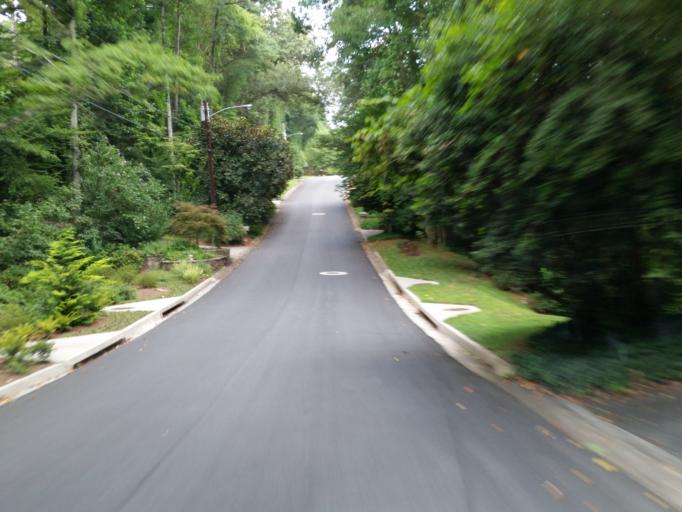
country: US
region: Georgia
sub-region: Cobb County
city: Vinings
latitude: 33.8638
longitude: -84.4620
